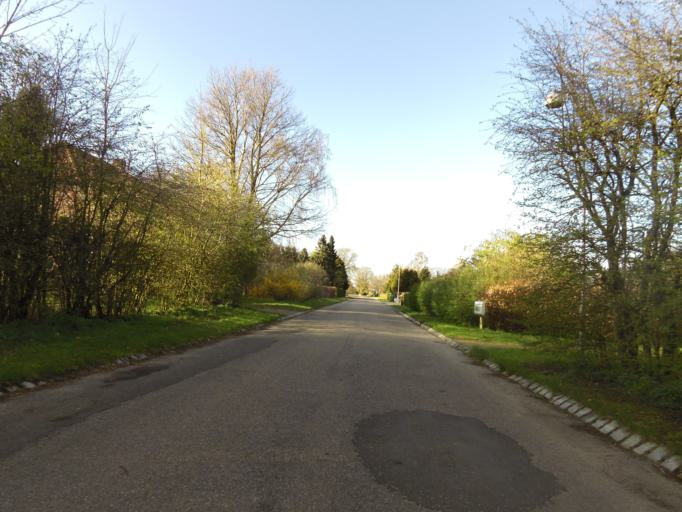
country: DK
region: South Denmark
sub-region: Tonder Kommune
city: Toftlund
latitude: 55.2322
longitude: 9.1238
